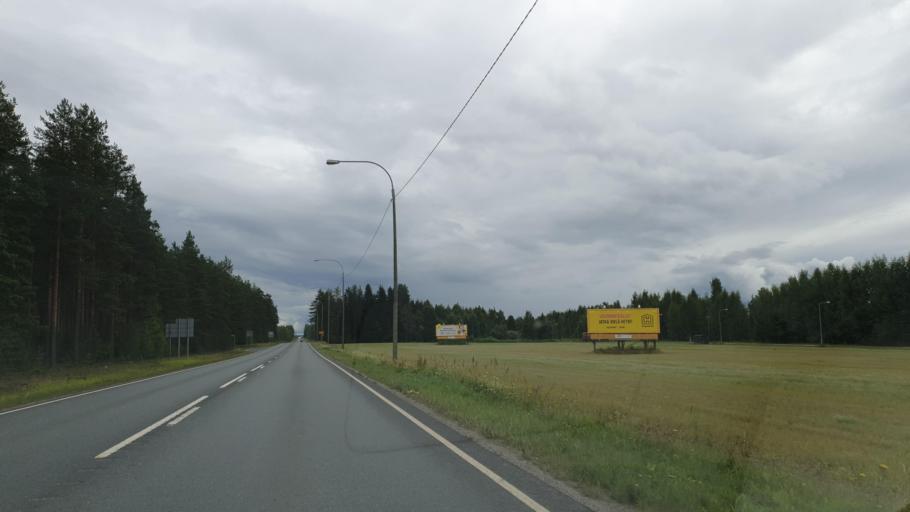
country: FI
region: Northern Savo
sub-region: Ylae-Savo
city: Lapinlahti
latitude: 63.3444
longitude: 27.4178
